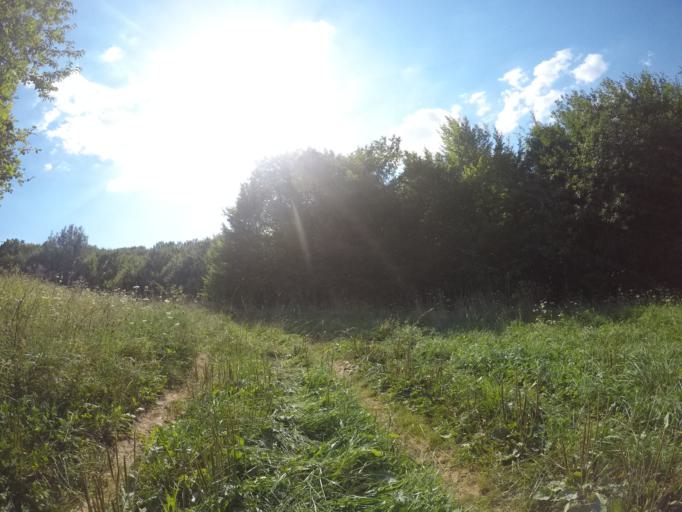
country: SK
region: Presovsky
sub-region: Okres Presov
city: Presov
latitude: 48.9412
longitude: 21.1670
